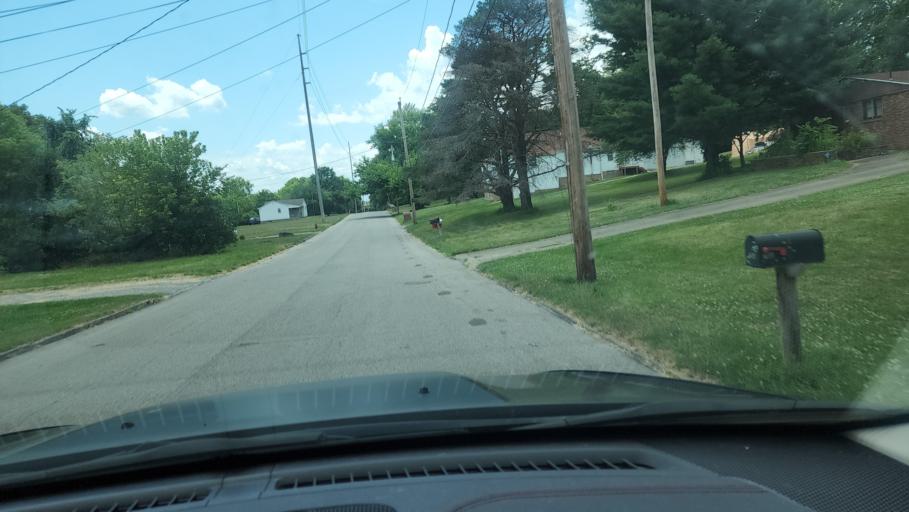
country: US
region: Ohio
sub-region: Mahoning County
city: Campbell
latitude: 41.0785
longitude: -80.5847
